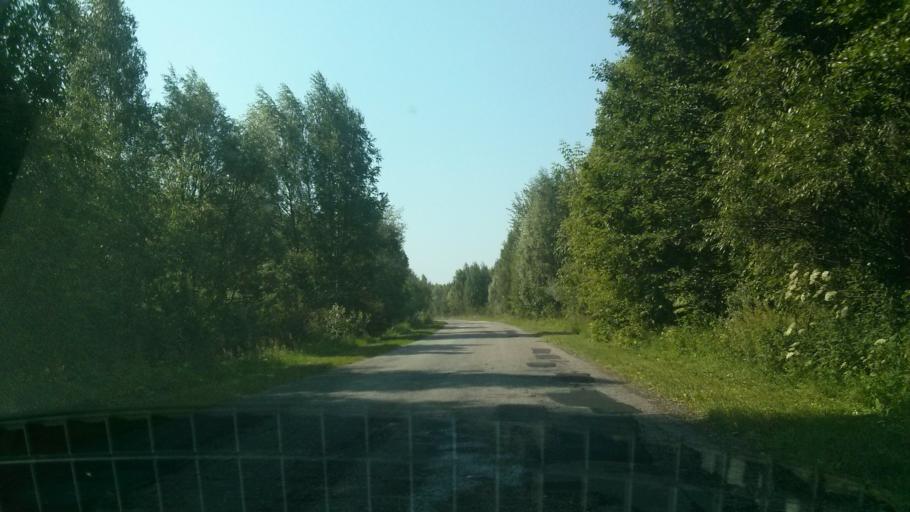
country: RU
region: Vladimir
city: Murom
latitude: 55.4949
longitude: 41.9762
